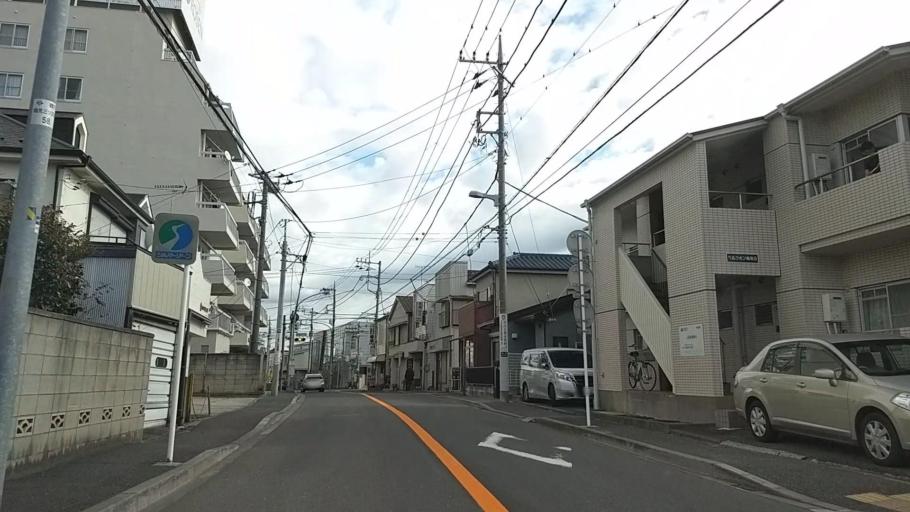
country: JP
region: Kanagawa
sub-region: Kawasaki-shi
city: Kawasaki
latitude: 35.5108
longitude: 139.6589
